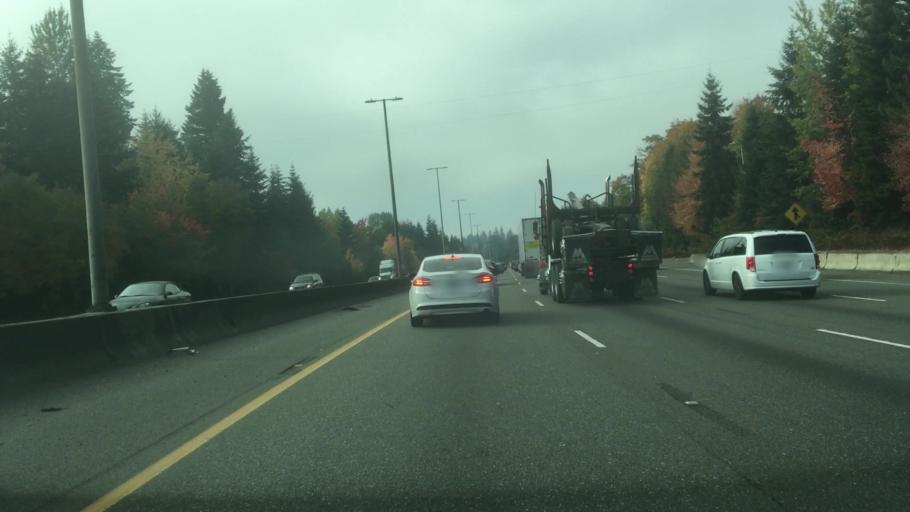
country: US
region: Washington
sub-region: Thurston County
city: Lacey
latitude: 47.0404
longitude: -122.8567
